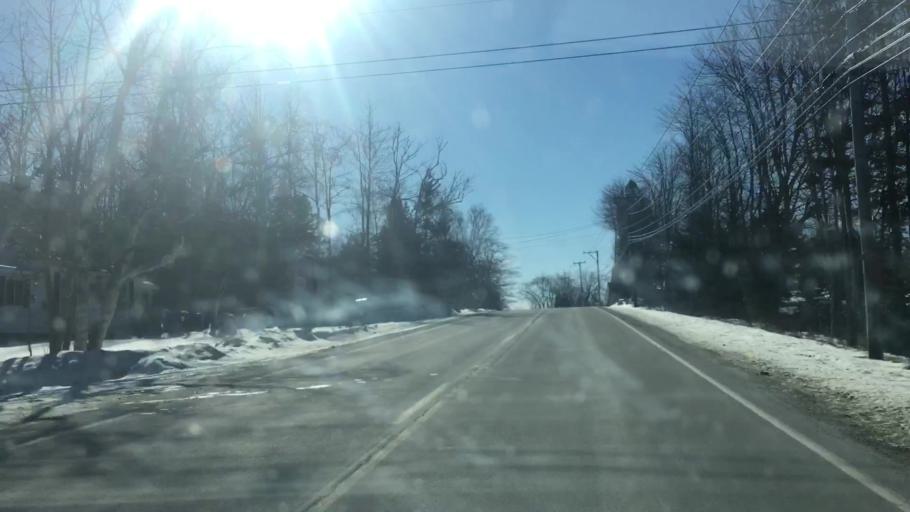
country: US
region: Maine
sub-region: Hancock County
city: Ellsworth
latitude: 44.5110
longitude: -68.4373
